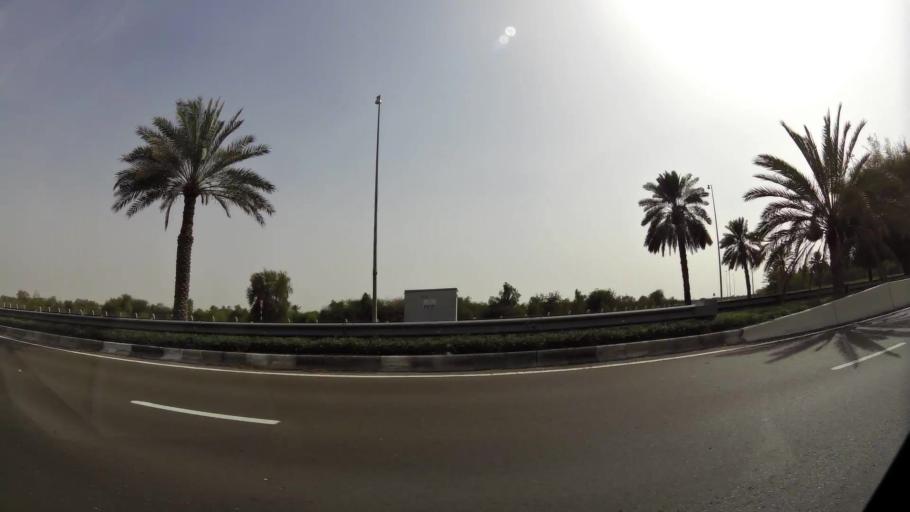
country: AE
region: Abu Dhabi
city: Al Ain
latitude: 24.1820
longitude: 55.5985
